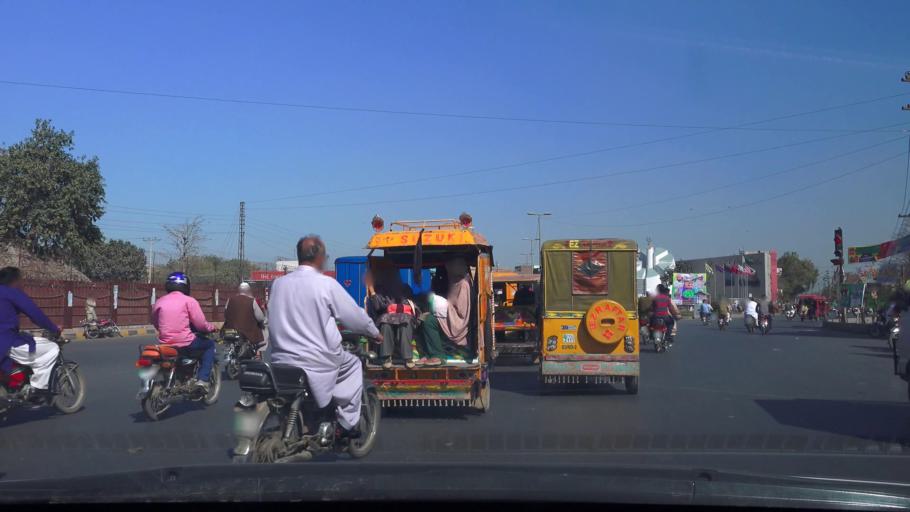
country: PK
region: Punjab
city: Faisalabad
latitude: 31.4119
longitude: 73.0619
